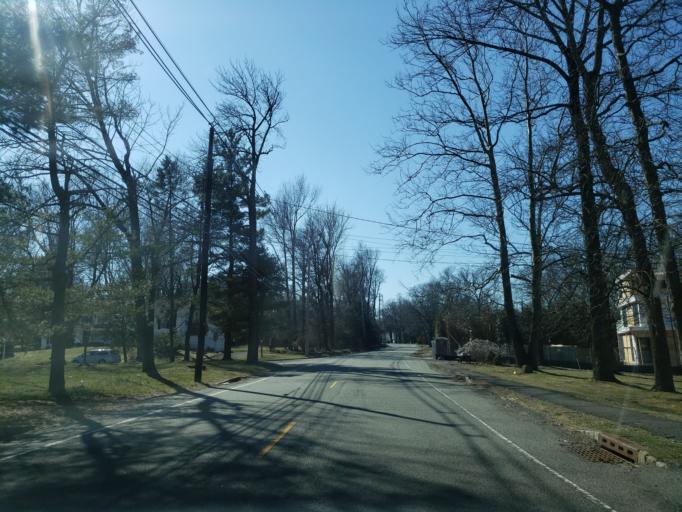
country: US
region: New Jersey
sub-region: Essex County
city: Short Hills
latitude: 40.7419
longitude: -74.3396
